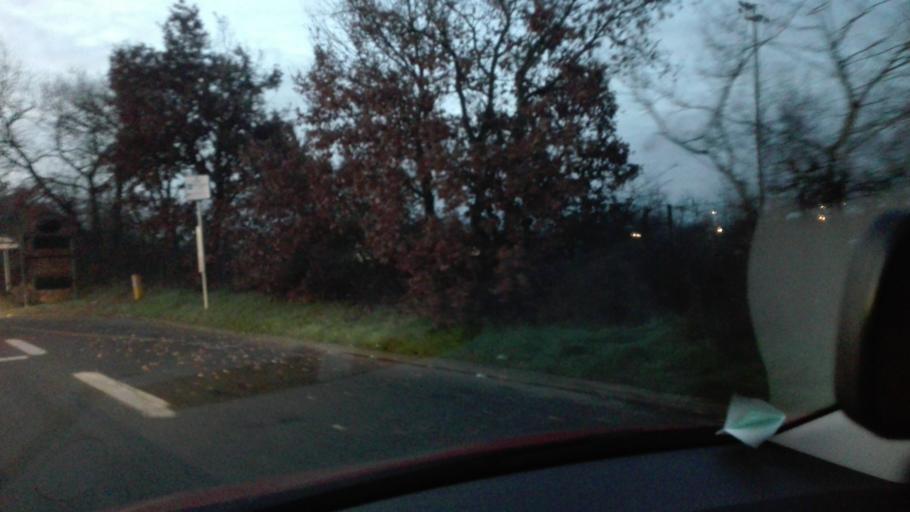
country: FR
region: Midi-Pyrenees
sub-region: Departement de la Haute-Garonne
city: Seilh
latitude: 43.6975
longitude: 1.3493
